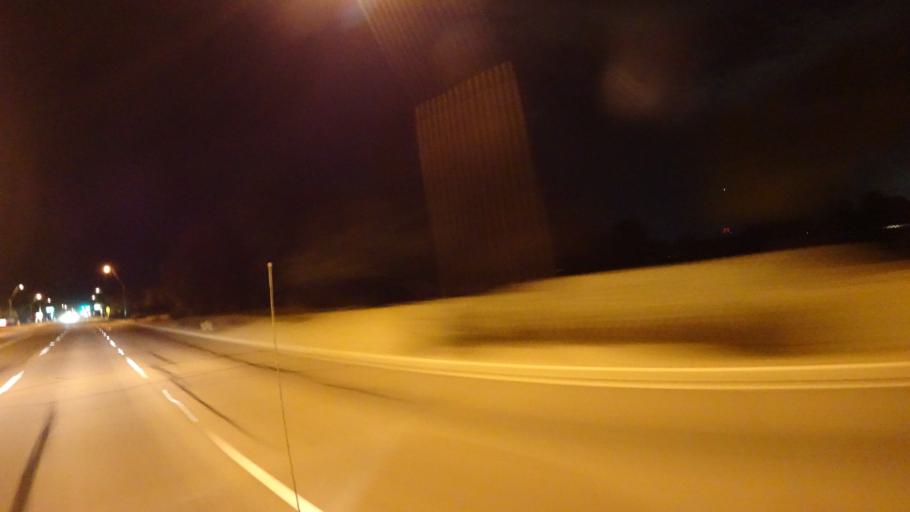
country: US
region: Arizona
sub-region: Maricopa County
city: Guadalupe
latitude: 33.3299
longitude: -111.9284
